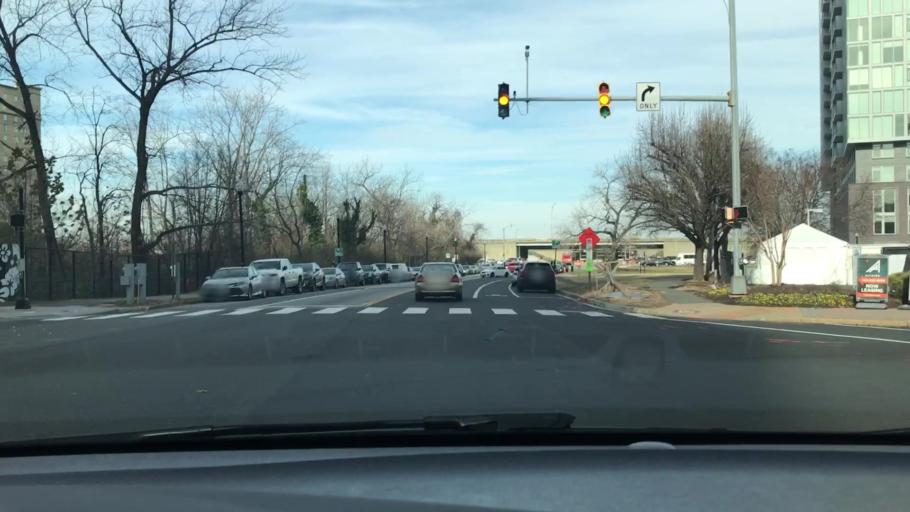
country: US
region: Washington, D.C.
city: Washington, D.C.
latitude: 38.8630
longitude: -77.0542
